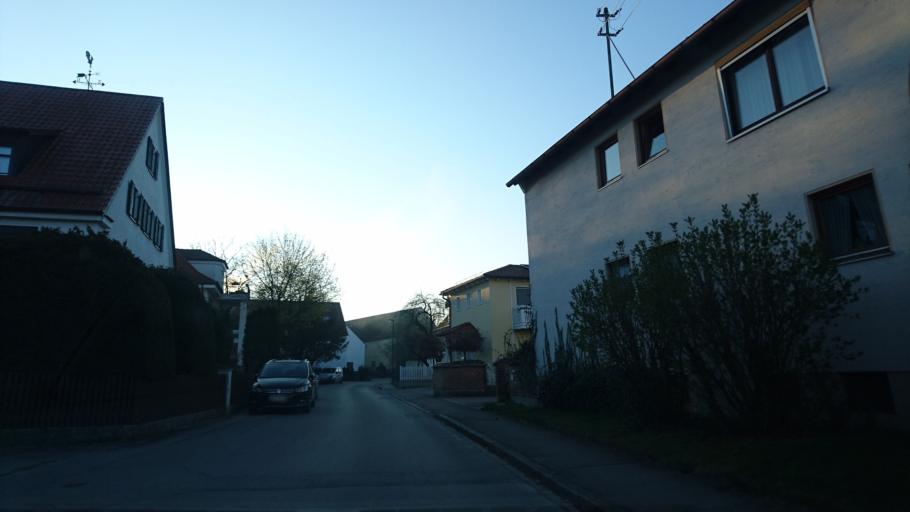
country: DE
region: Bavaria
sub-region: Swabia
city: Diedorf
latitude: 48.3552
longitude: 10.7731
